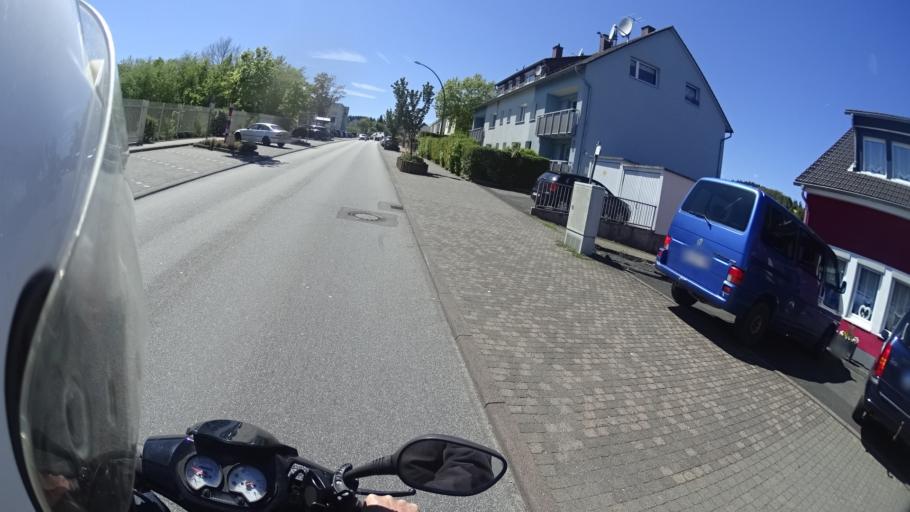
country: DE
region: Hesse
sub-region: Regierungsbezirk Darmstadt
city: Bad Schwalbach
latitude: 50.1431
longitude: 8.0656
